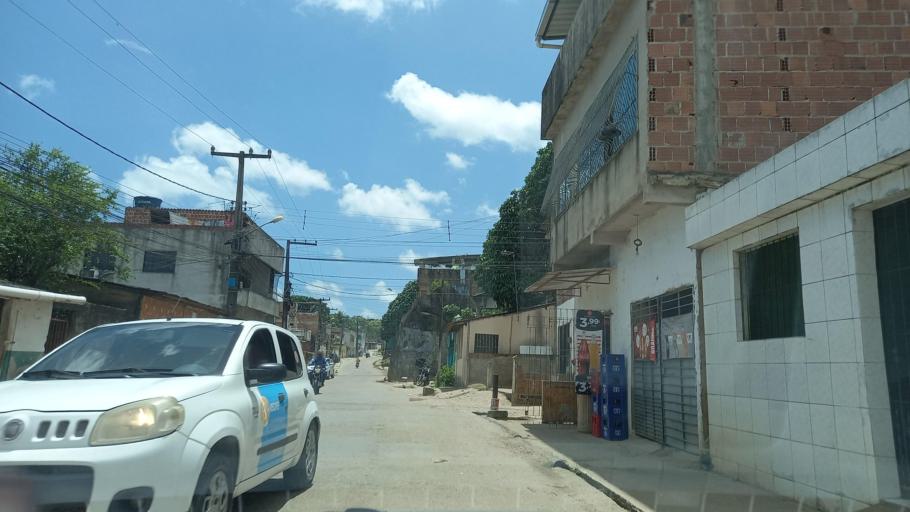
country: BR
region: Pernambuco
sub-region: Jaboatao Dos Guararapes
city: Jaboatao
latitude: -8.1719
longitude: -35.0041
